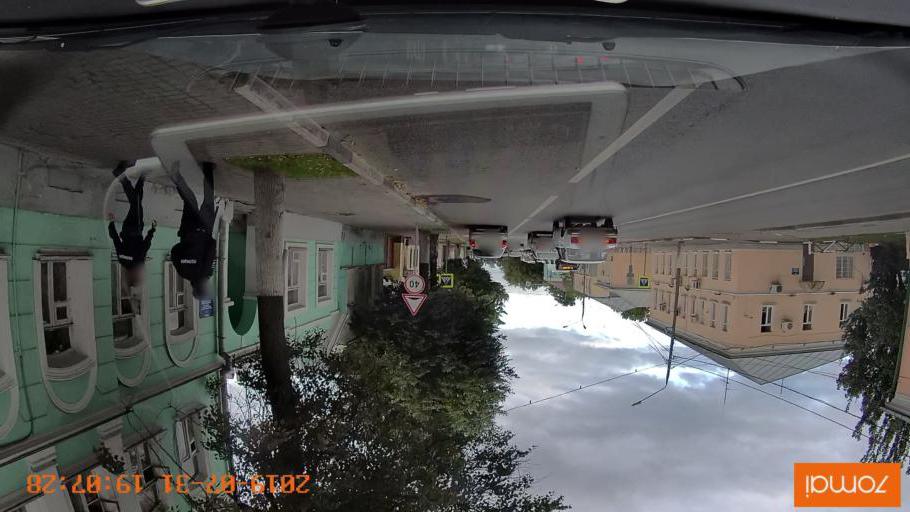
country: RU
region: Moskovskaya
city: Kolomna
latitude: 55.0981
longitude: 38.7608
